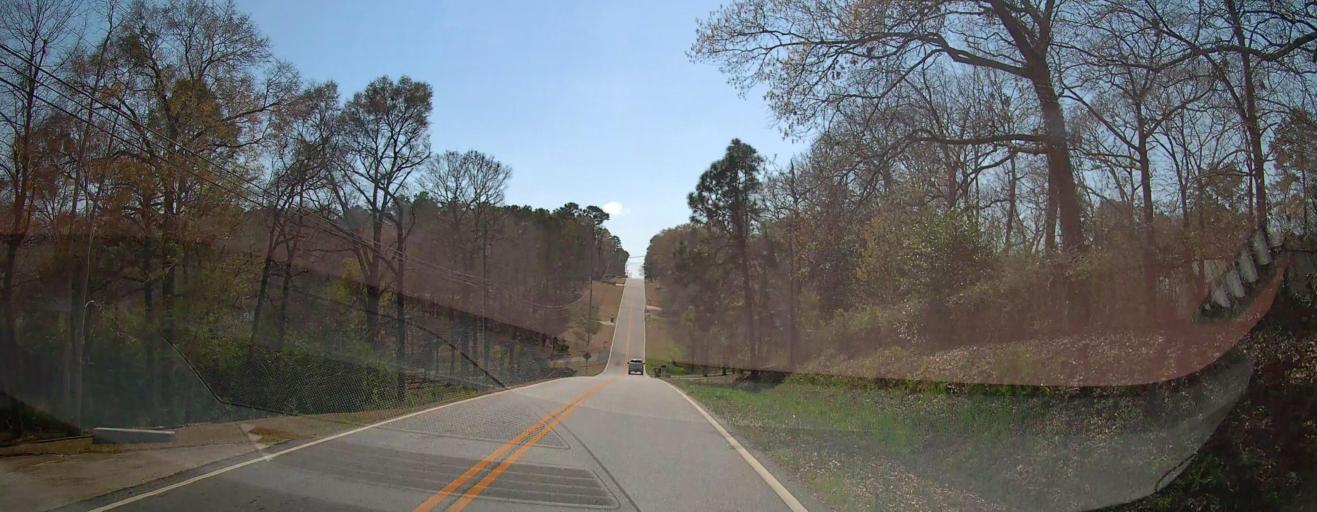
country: US
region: Georgia
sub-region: Houston County
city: Centerville
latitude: 32.5926
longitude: -83.6944
